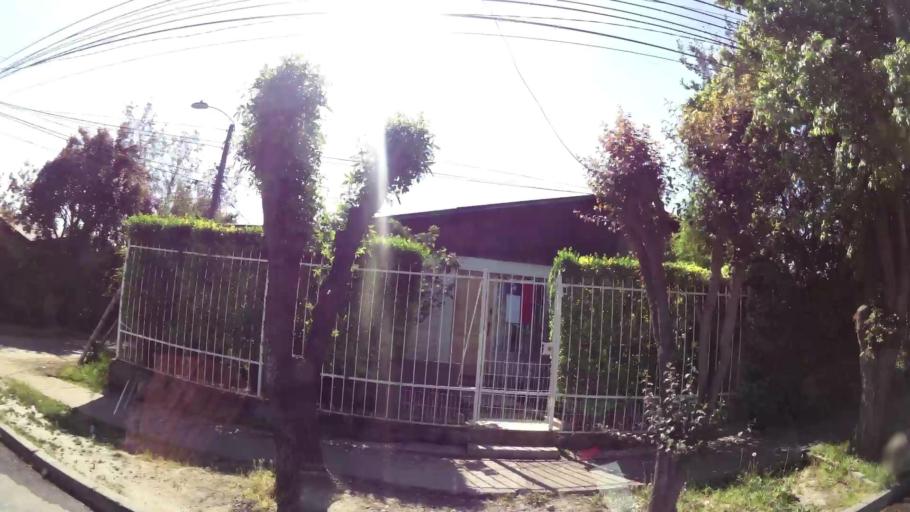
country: CL
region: Santiago Metropolitan
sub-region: Provincia de Santiago
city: Villa Presidente Frei, Nunoa, Santiago, Chile
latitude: -33.5283
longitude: -70.5637
